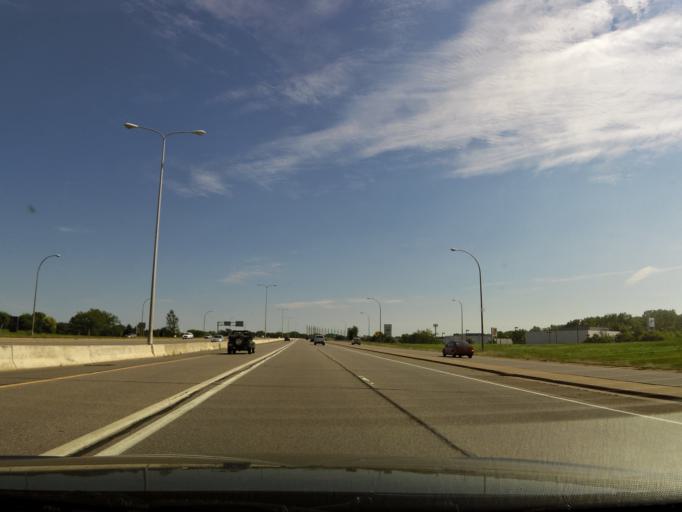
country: US
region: Minnesota
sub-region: Hennepin County
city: Minnetonka Mills
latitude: 44.9734
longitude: -93.3992
